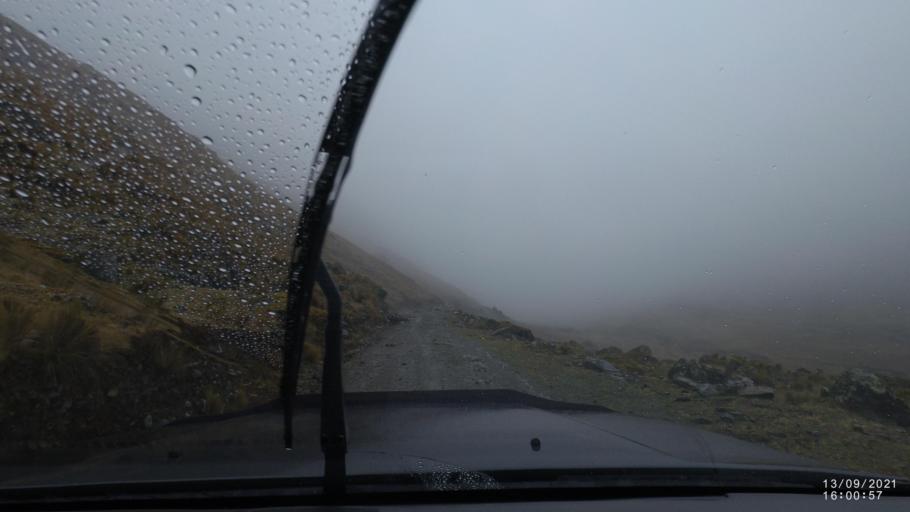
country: BO
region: Cochabamba
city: Colomi
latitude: -17.2953
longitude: -65.7101
